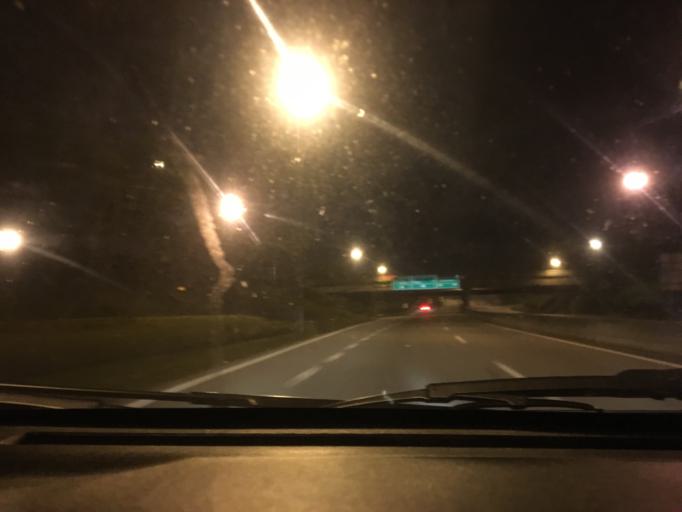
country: MY
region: Selangor
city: Kampong Baharu Balakong
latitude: 2.9826
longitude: 101.7324
